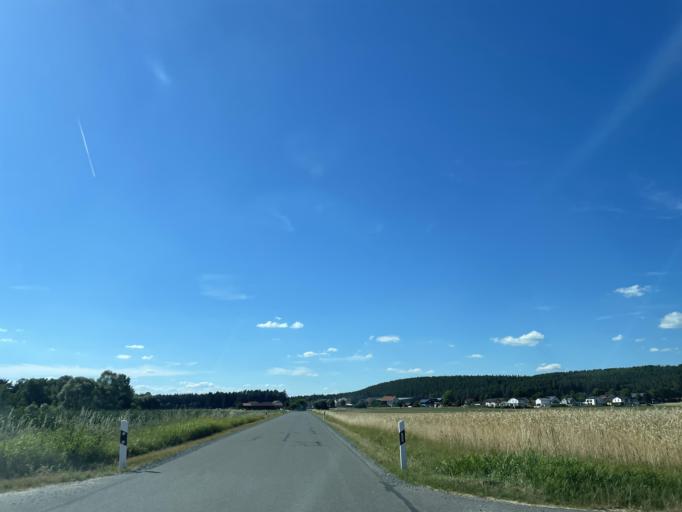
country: DE
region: Bavaria
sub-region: Upper Palatinate
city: Trabitz
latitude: 49.7694
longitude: 11.8641
